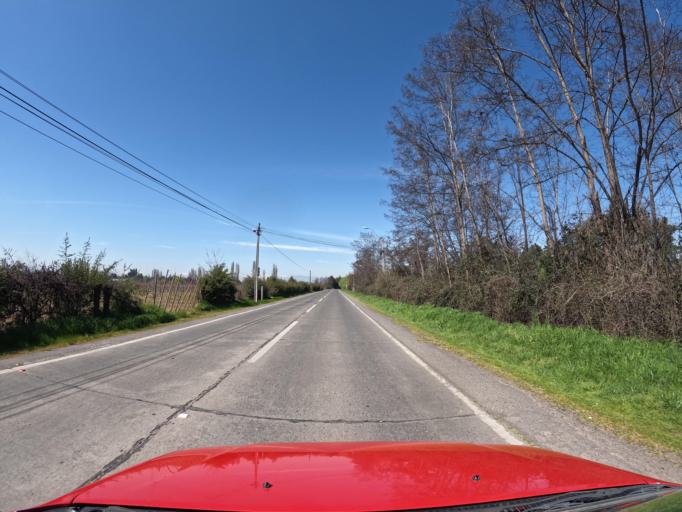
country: CL
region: Maule
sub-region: Provincia de Curico
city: Rauco
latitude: -35.0072
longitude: -71.3189
